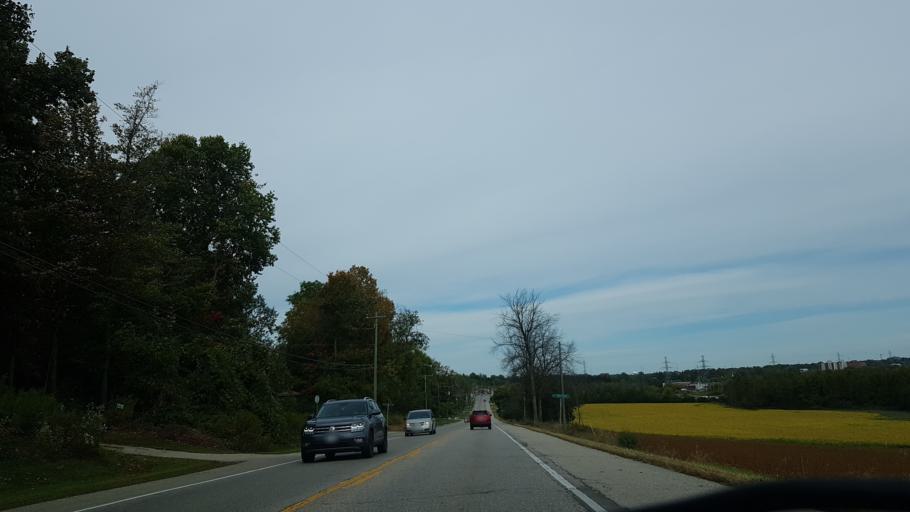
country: CA
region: Ontario
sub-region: Wellington County
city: Guelph
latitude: 43.5124
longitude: -80.2669
